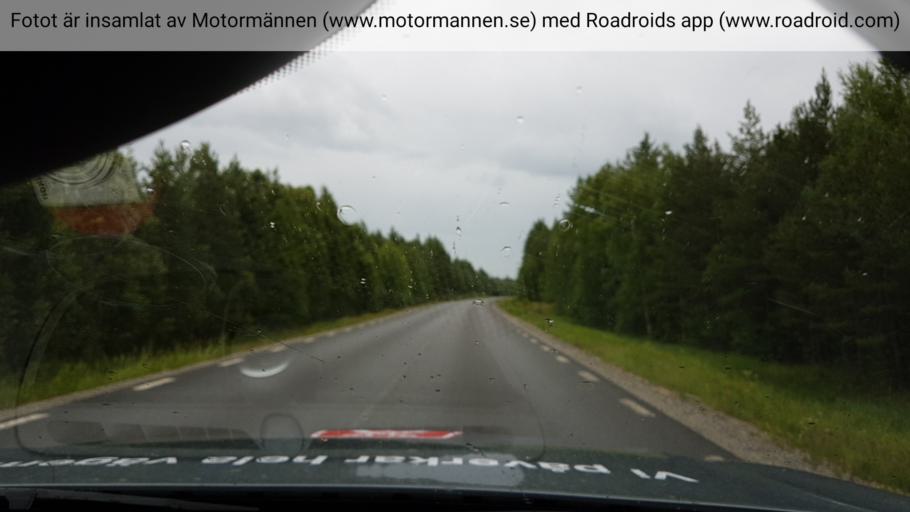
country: SE
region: Jaemtland
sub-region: Braecke Kommun
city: Braecke
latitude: 62.4500
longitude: 14.9789
